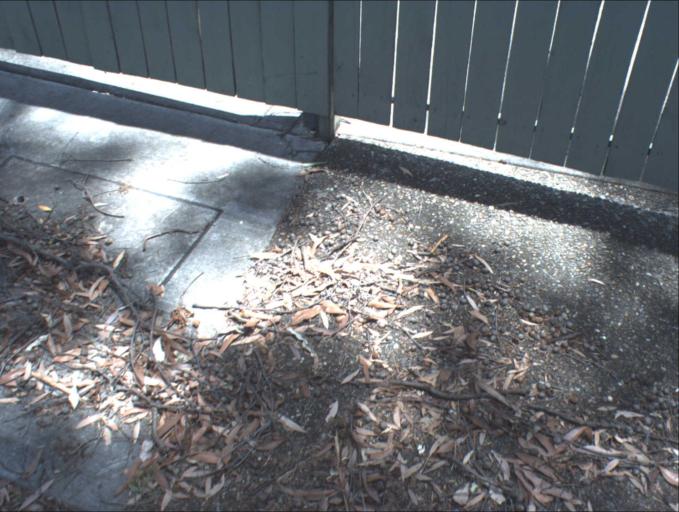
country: AU
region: Queensland
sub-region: Logan
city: Beenleigh
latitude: -27.7062
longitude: 153.2118
